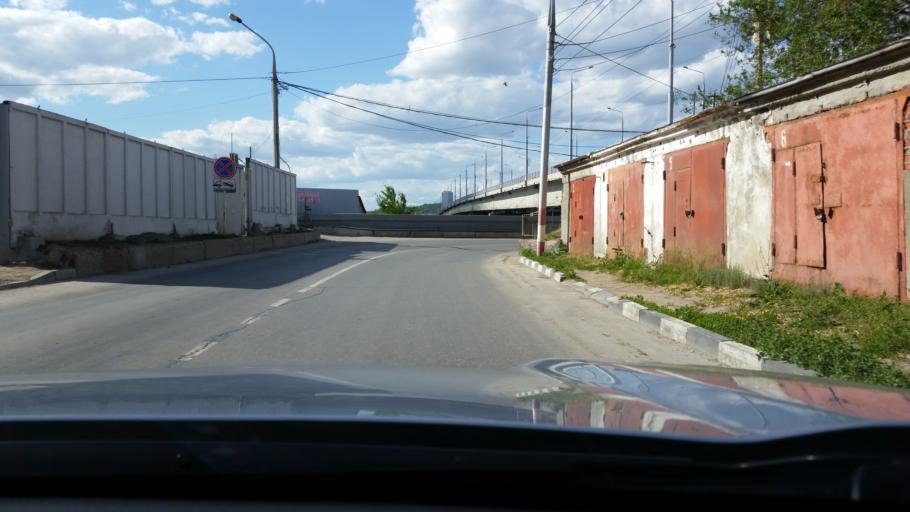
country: RU
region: Saratov
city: Engel's
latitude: 51.5053
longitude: 46.0778
